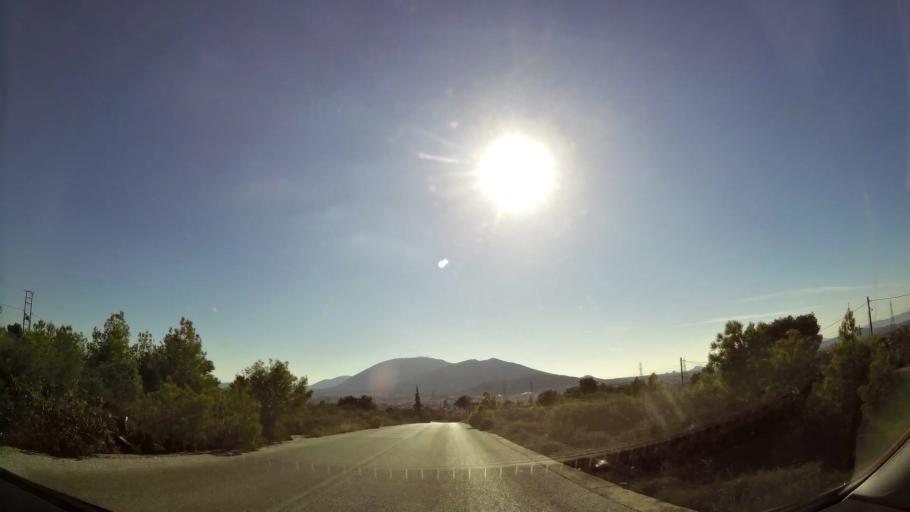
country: GR
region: Attica
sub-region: Nomarchia Anatolikis Attikis
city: Anthousa
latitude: 38.0282
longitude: 23.8698
